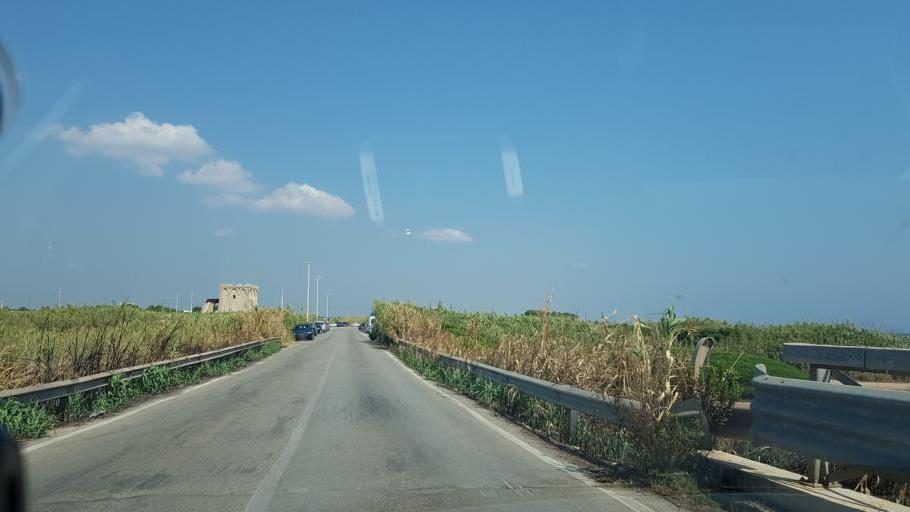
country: IT
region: Apulia
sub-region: Provincia di Taranto
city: Maruggio
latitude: 40.3039
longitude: 17.6326
